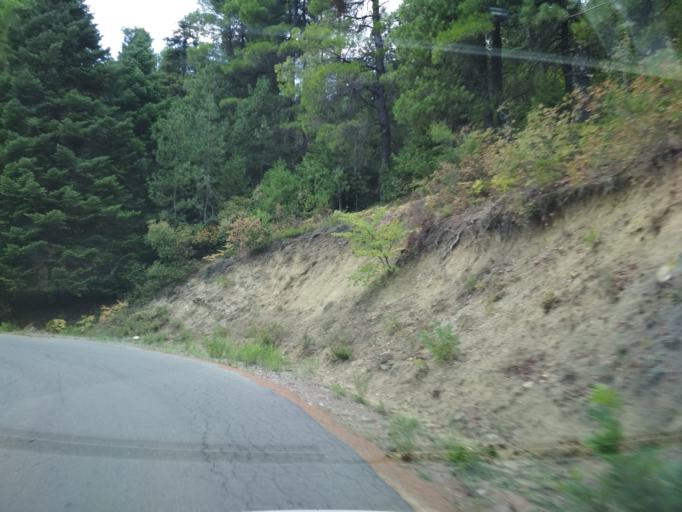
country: GR
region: Central Greece
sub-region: Nomos Evvoias
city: Roviai
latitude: 38.8568
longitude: 23.2858
